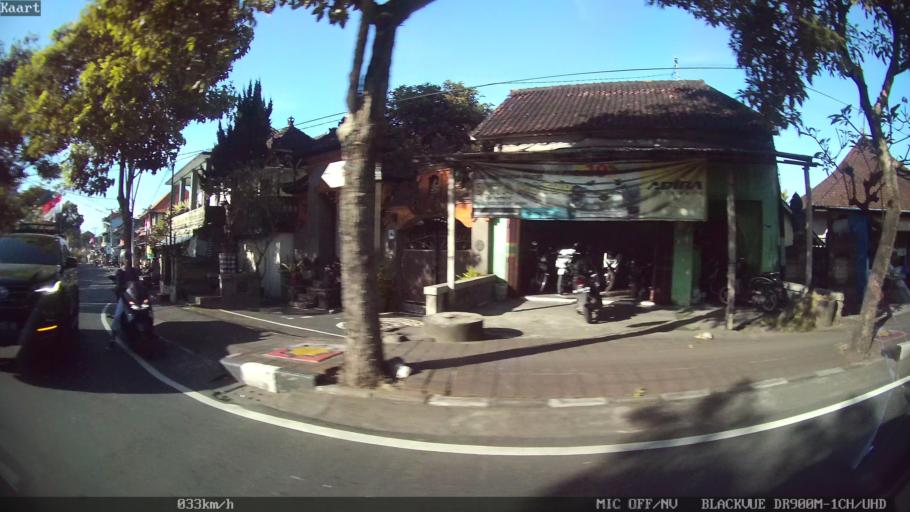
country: ID
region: Bali
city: Banjar Karangsuling
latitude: -8.6080
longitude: 115.1883
